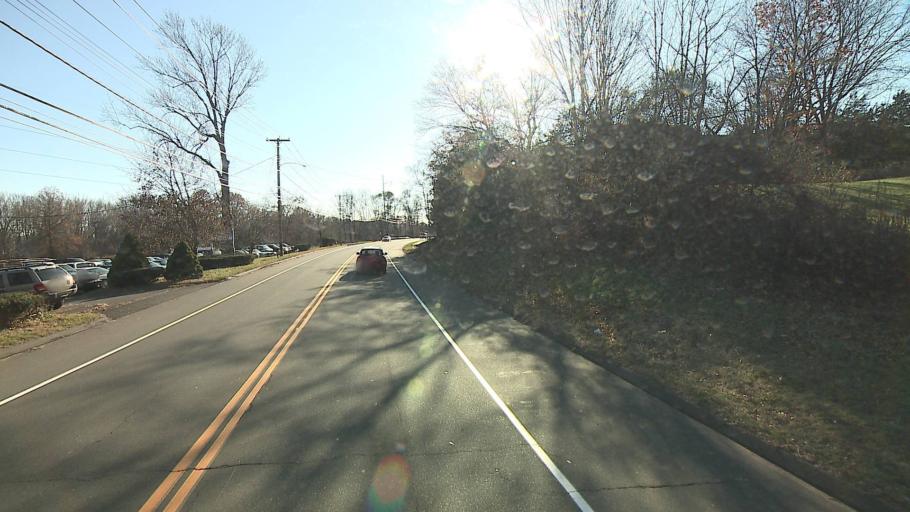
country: US
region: Connecticut
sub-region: New Haven County
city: North Haven
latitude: 41.3847
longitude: -72.8747
